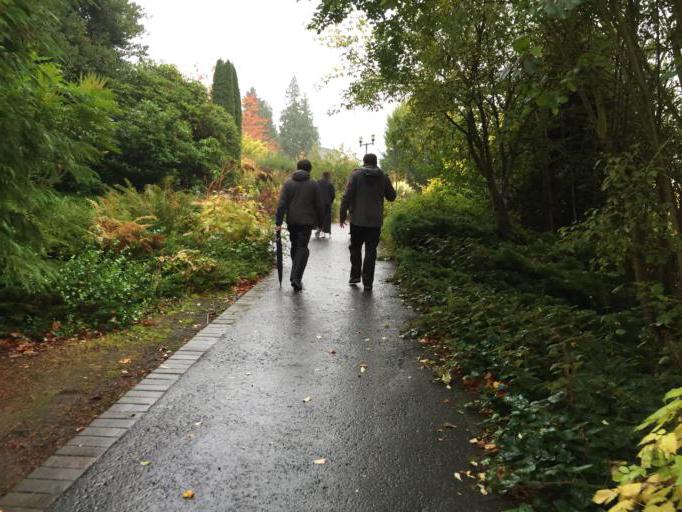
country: GB
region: Scotland
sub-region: Perth and Kinross
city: Perth
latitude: 56.3946
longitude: -3.4233
